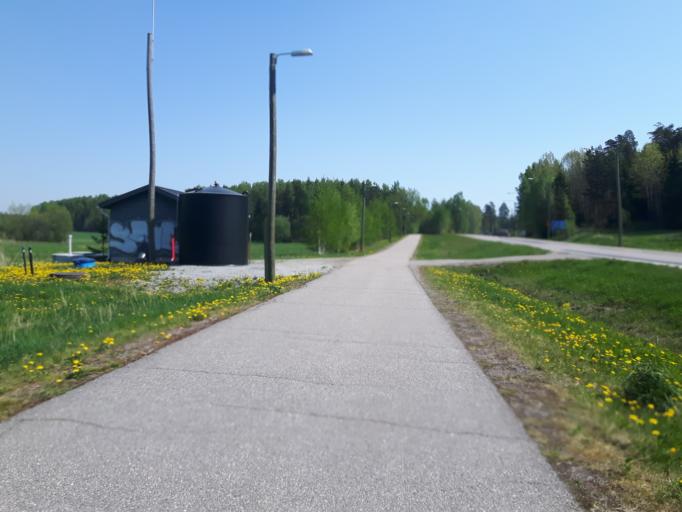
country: FI
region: Uusimaa
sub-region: Helsinki
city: Sibbo
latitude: 60.2587
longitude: 25.2030
